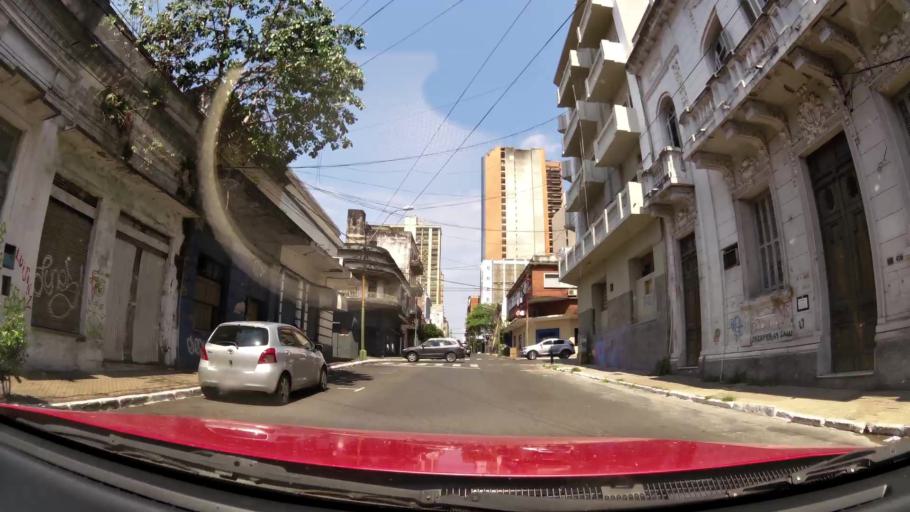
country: PY
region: Asuncion
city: Asuncion
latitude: -25.2796
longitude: -57.6407
